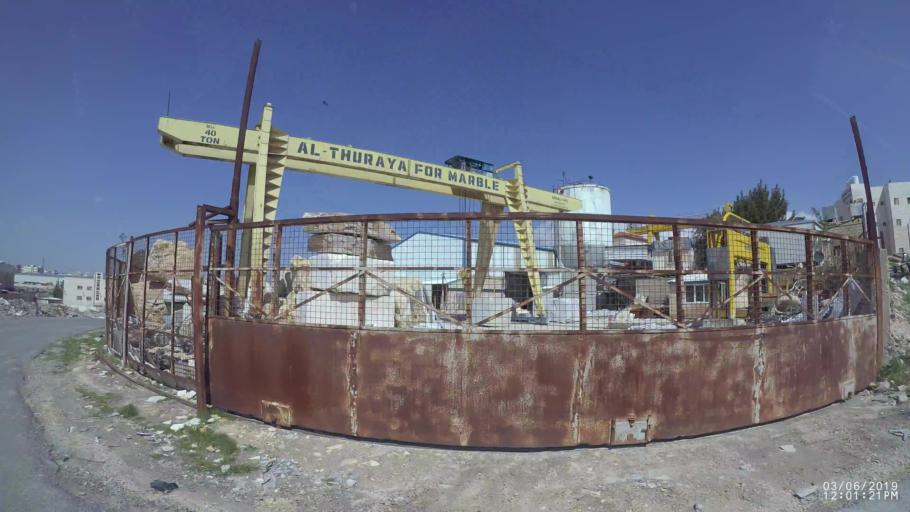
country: JO
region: Zarqa
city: Russeifa
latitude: 31.9863
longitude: 36.0138
